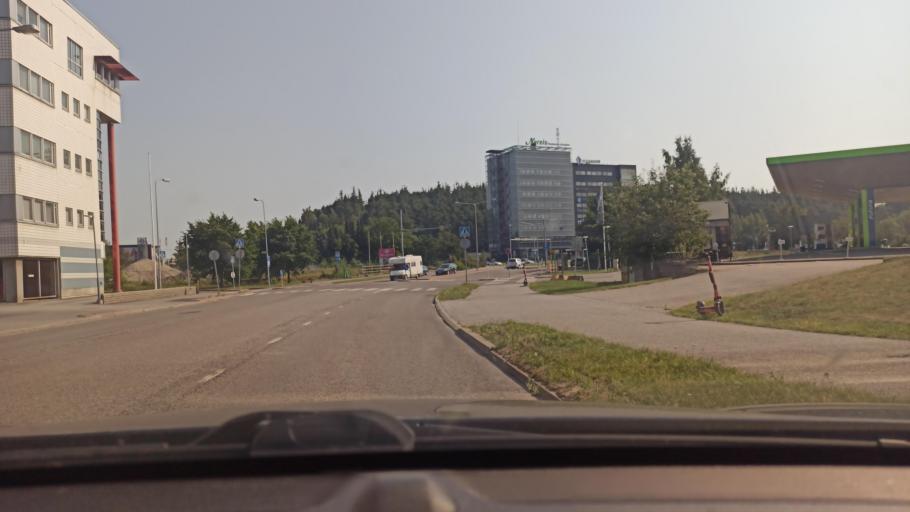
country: FI
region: Varsinais-Suomi
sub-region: Turku
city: Turku
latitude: 60.4579
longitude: 22.2363
